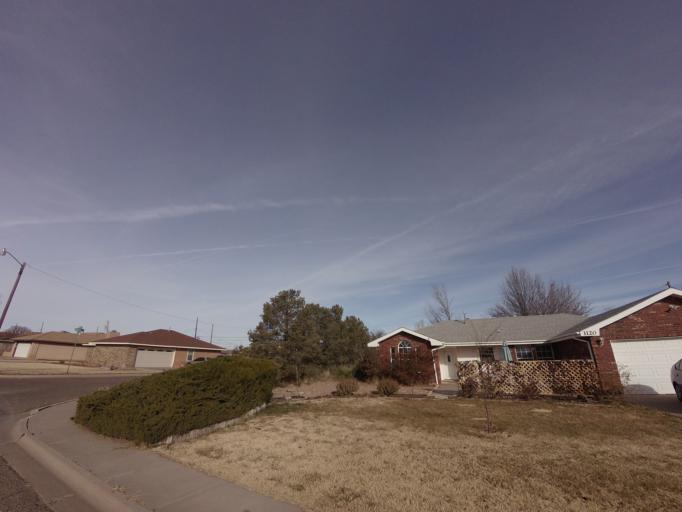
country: US
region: New Mexico
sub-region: Curry County
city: Clovis
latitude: 34.4161
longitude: -103.2294
